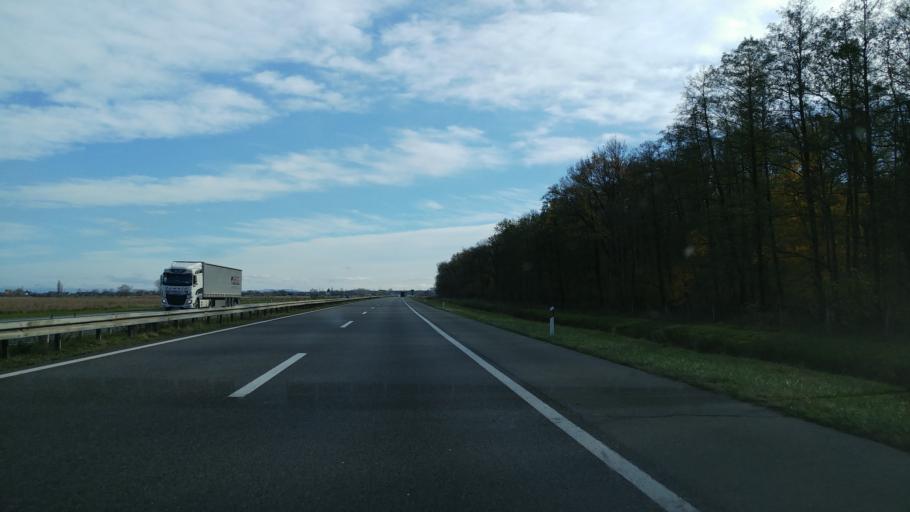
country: HR
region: Sisacko-Moslavacka
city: Repusnica
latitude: 45.4715
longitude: 16.7393
